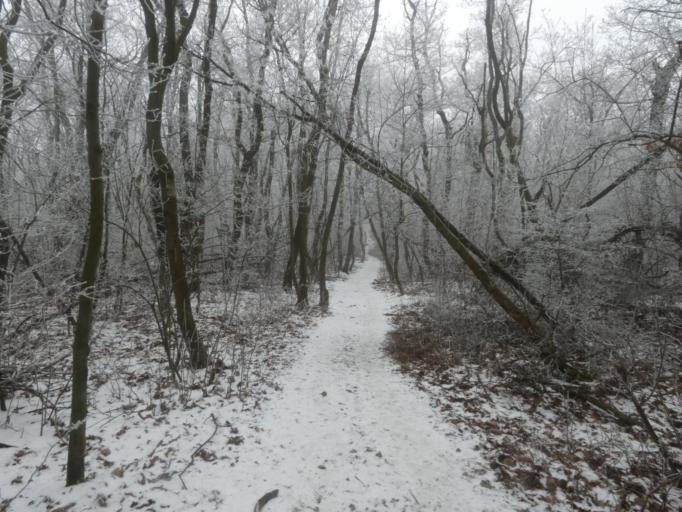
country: HU
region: Pest
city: Urom
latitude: 47.5600
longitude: 18.9952
